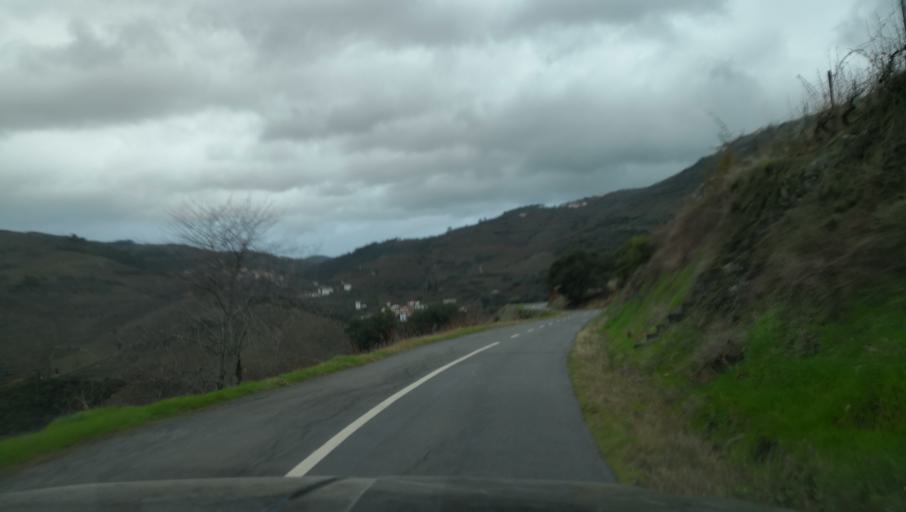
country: PT
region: Vila Real
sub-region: Santa Marta de Penaguiao
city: Santa Marta de Penaguiao
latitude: 41.2252
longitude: -7.7471
